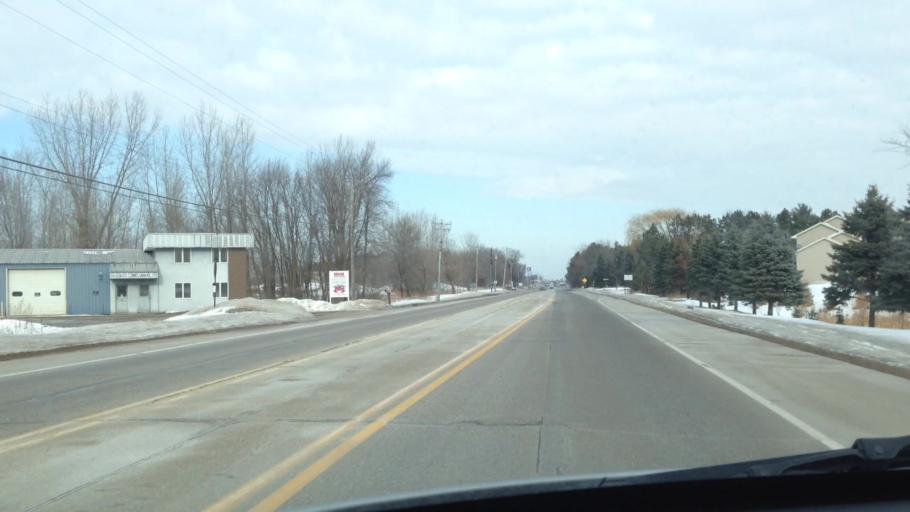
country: US
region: Minnesota
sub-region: Anoka County
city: Lino Lakes
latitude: 45.1711
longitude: -93.1190
